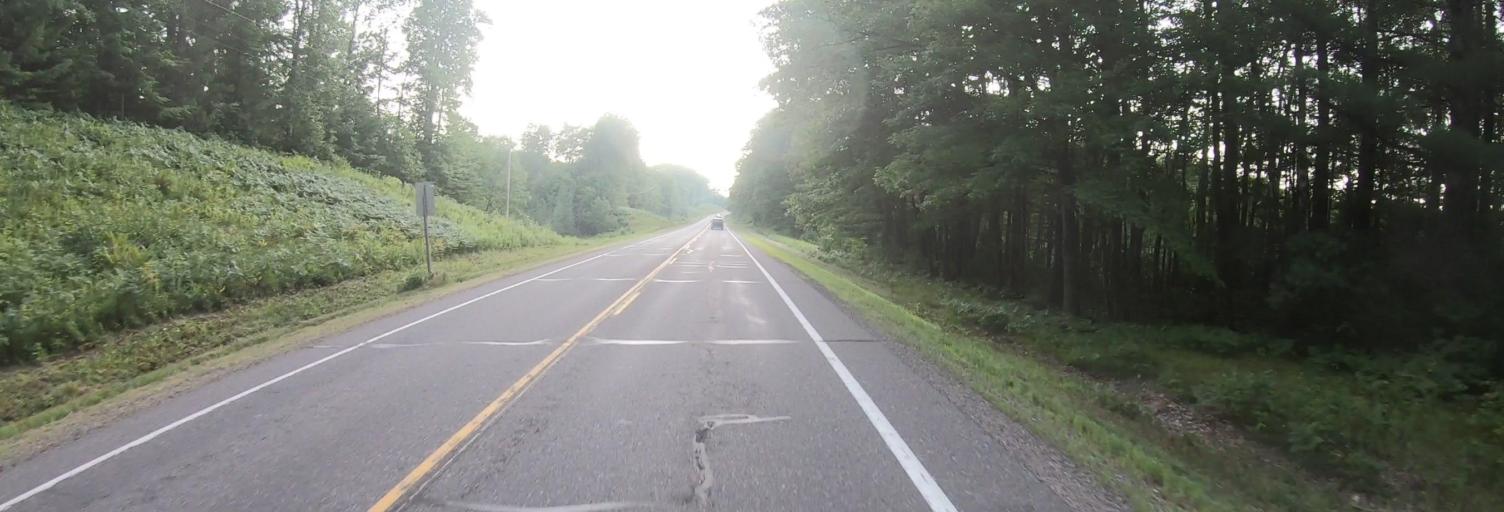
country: US
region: Wisconsin
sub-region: Sawyer County
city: Little Round Lake
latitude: 46.0654
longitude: -91.1395
